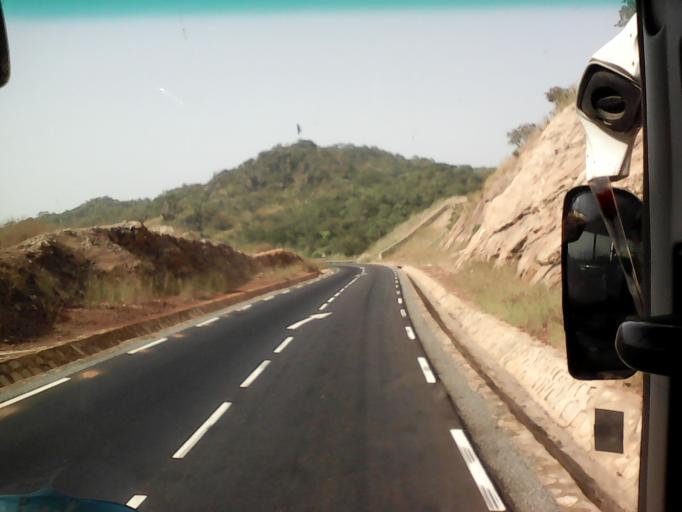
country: TG
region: Kara
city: Bafilo
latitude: 9.2675
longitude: 1.2339
